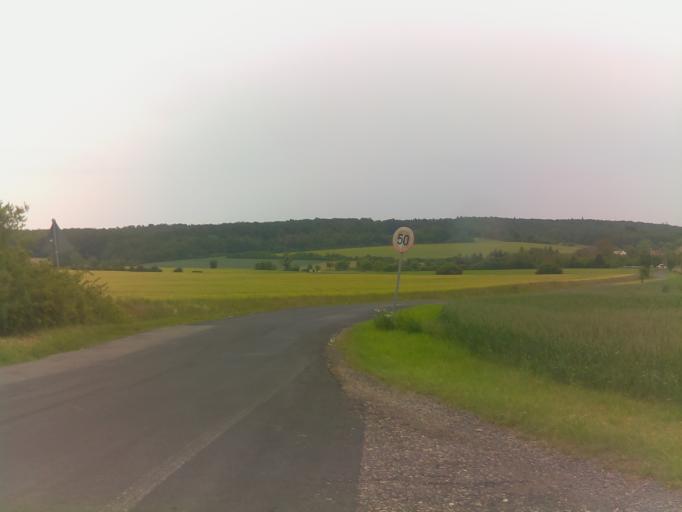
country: DE
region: Thuringia
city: Henneberg
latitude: 50.4512
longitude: 10.3635
